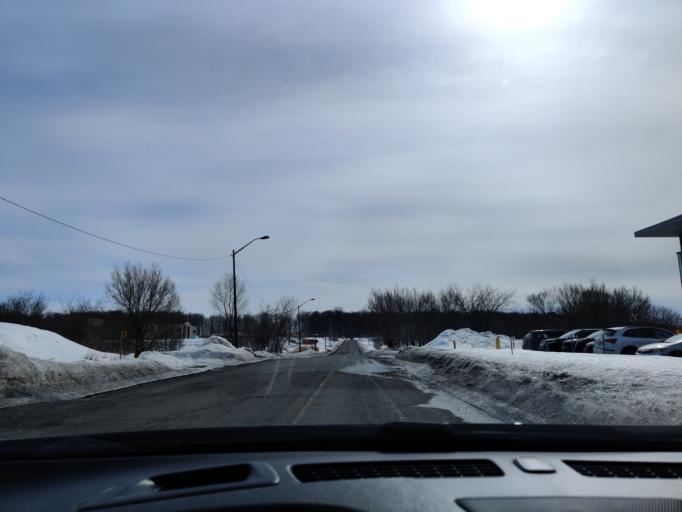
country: CA
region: Quebec
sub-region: Laurentides
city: Saint-Jerome
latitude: 45.7560
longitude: -73.9917
